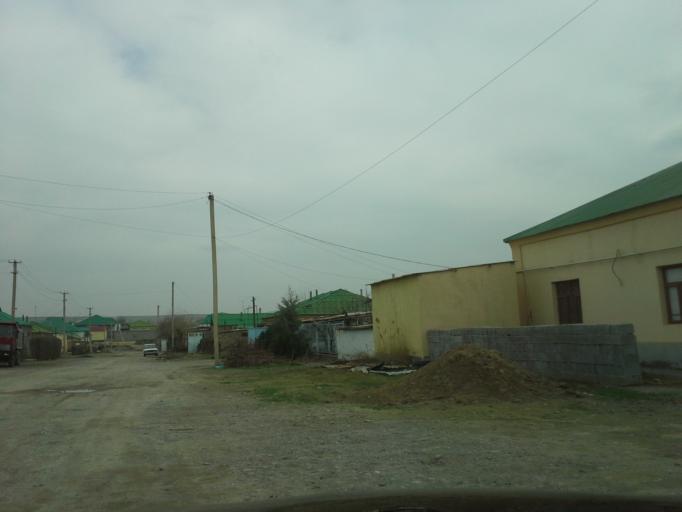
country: TM
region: Ahal
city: Abadan
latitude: 37.9744
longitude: 58.2196
